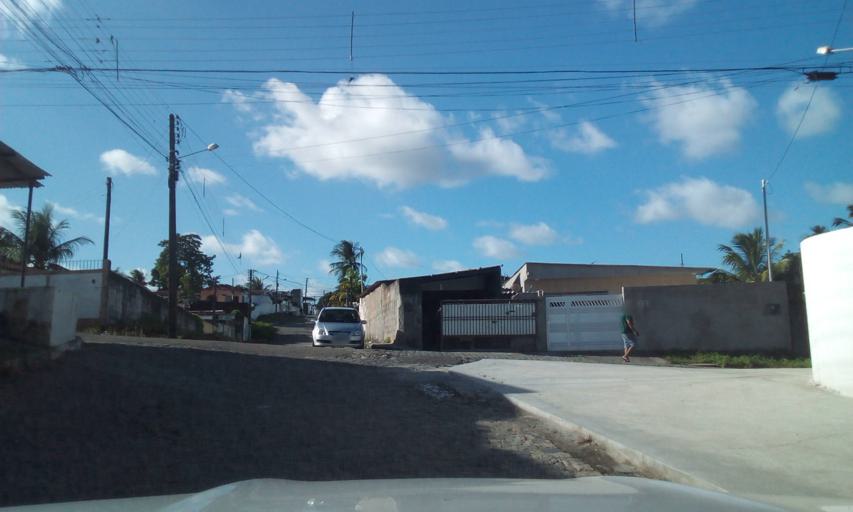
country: BR
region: Paraiba
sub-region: Joao Pessoa
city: Joao Pessoa
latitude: -7.1529
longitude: -34.8923
